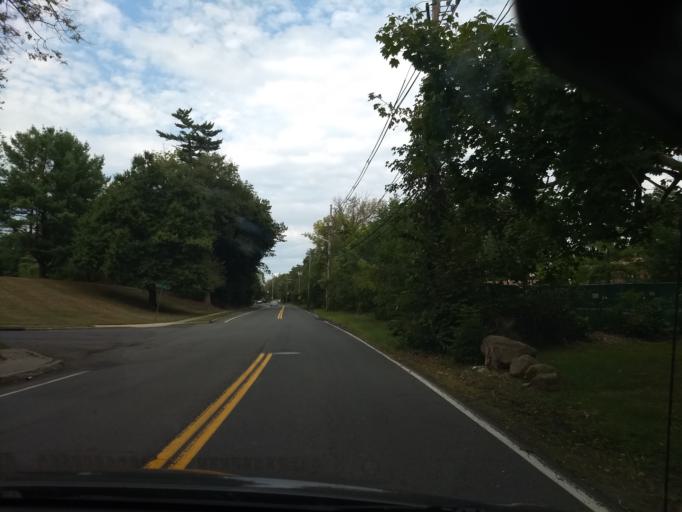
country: US
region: New York
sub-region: Rockland County
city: Spring Valley
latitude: 41.0976
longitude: -74.0331
